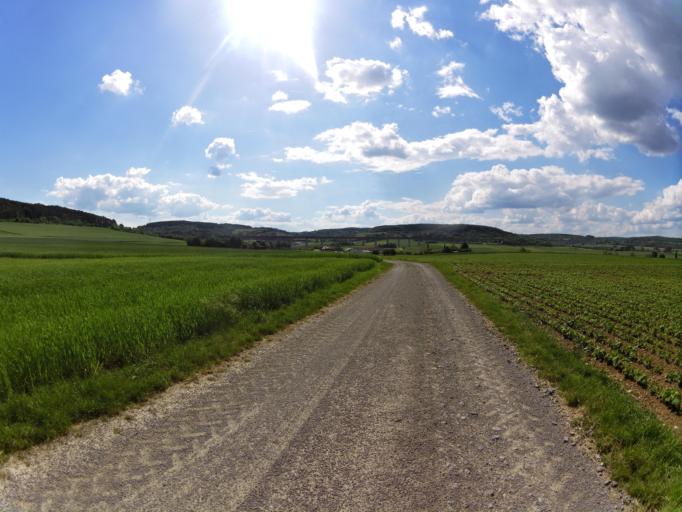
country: DE
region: Bavaria
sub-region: Regierungsbezirk Unterfranken
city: Zellingen
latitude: 49.8780
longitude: 9.8124
